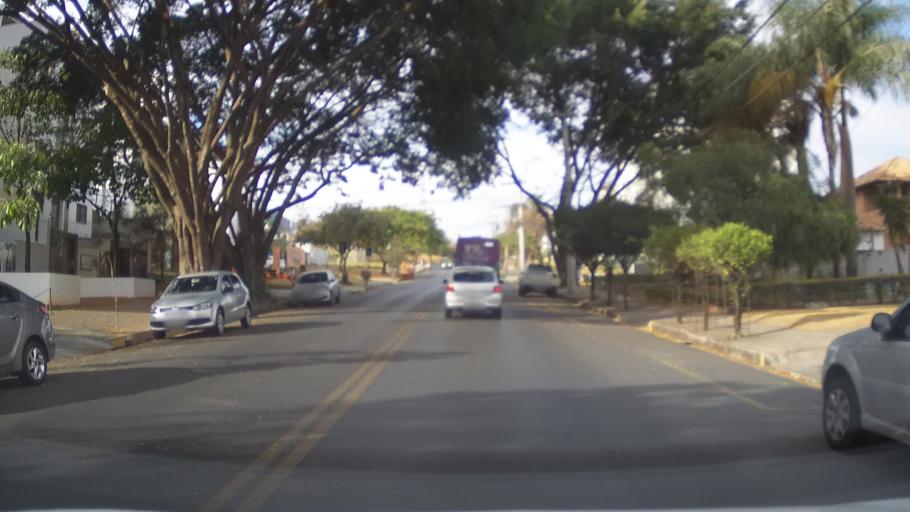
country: BR
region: Minas Gerais
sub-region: Belo Horizonte
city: Belo Horizonte
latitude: -19.8805
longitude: -43.9983
